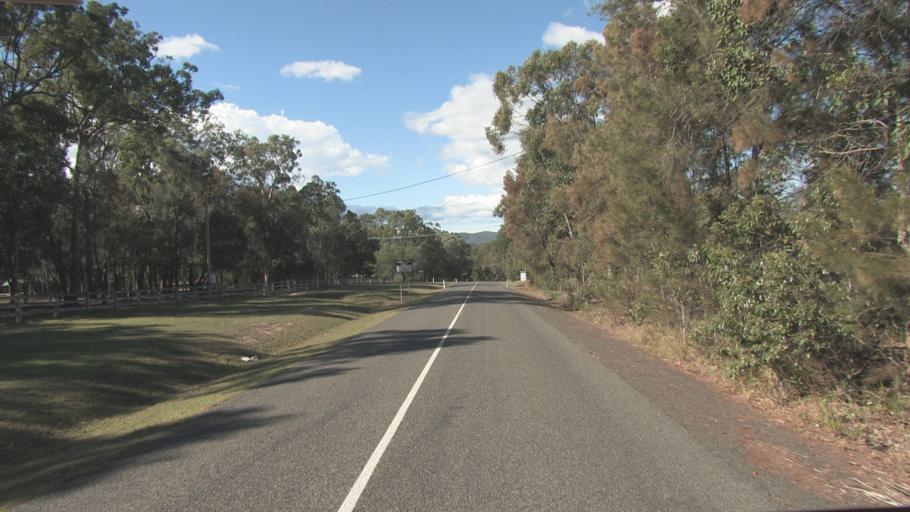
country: AU
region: Queensland
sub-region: Logan
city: Chambers Flat
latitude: -27.7914
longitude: 153.0839
